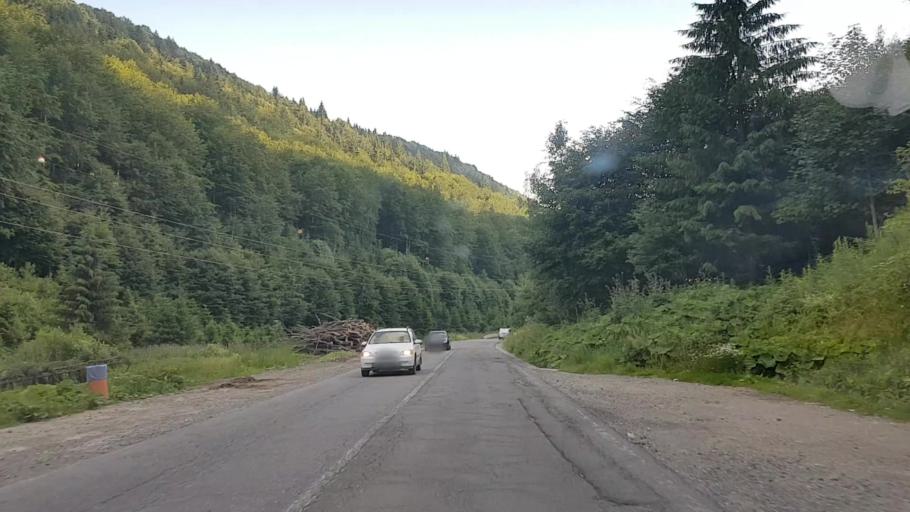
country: RO
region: Harghita
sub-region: Comuna Praid
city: Ocna de Sus
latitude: 46.6208
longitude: 25.2509
